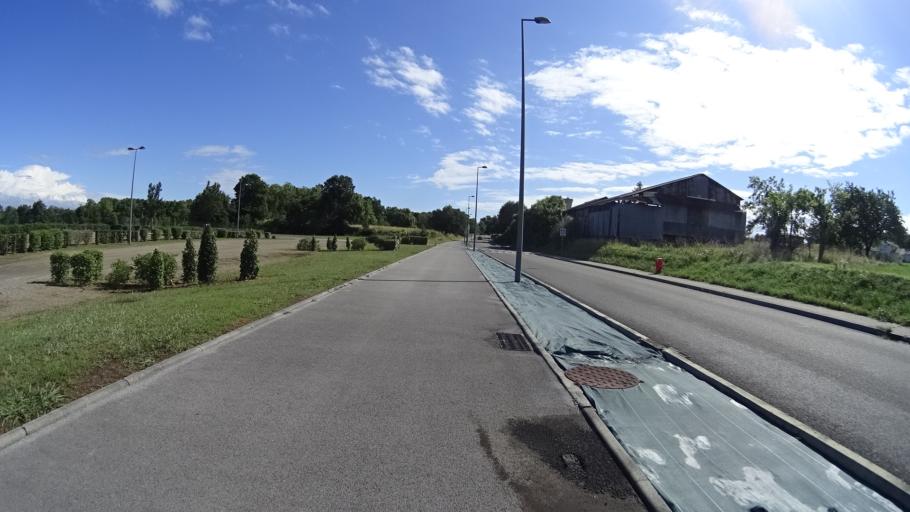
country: FR
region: Aquitaine
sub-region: Departement des Landes
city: Oeyreluy
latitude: 43.6950
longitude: -1.0796
